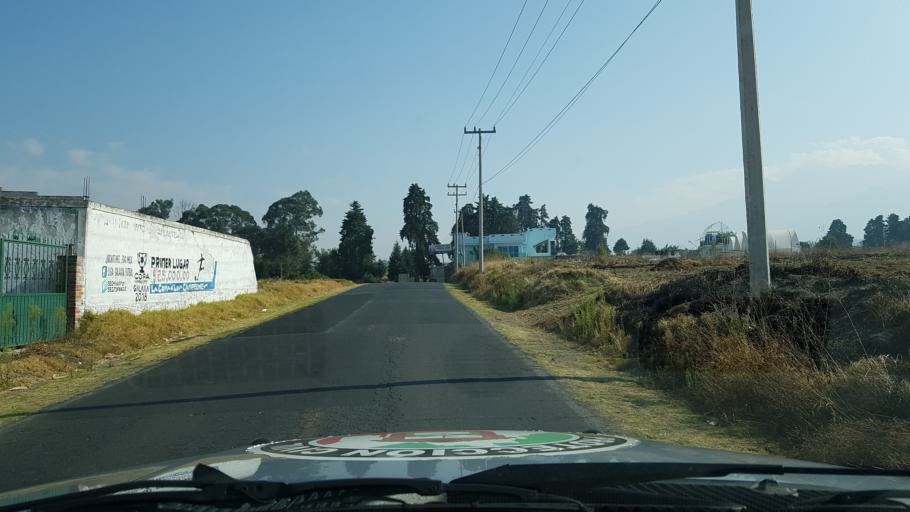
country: MX
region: Mexico
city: Atlautla
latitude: 19.0437
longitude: -98.7737
